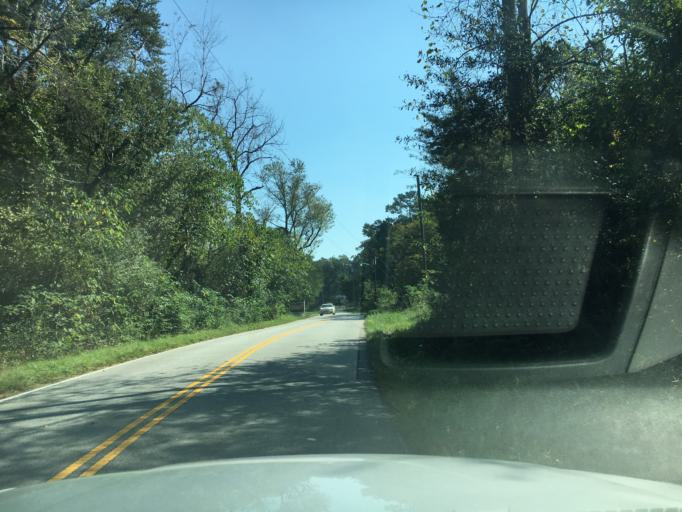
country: US
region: South Carolina
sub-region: Spartanburg County
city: Wellford
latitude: 34.9261
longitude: -82.1067
